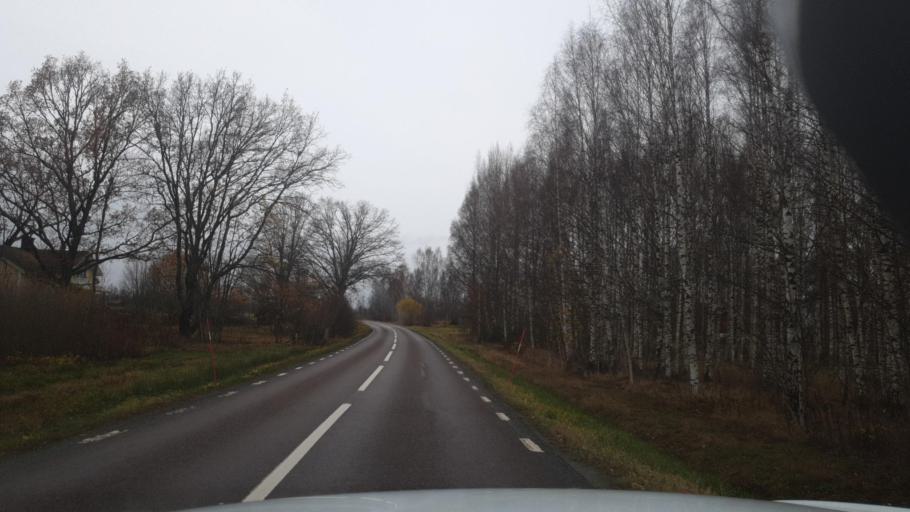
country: SE
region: Vaermland
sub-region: Arvika Kommun
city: Arvika
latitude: 59.6041
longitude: 12.5339
